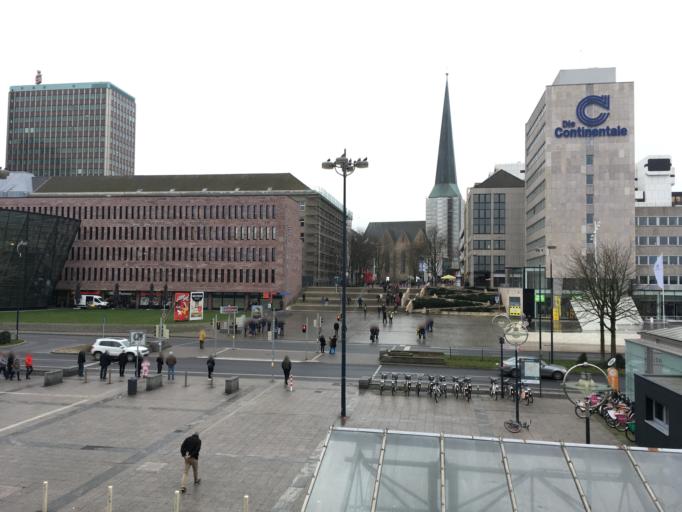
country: DE
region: North Rhine-Westphalia
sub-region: Regierungsbezirk Arnsberg
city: Dortmund
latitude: 51.5171
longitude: 7.4593
